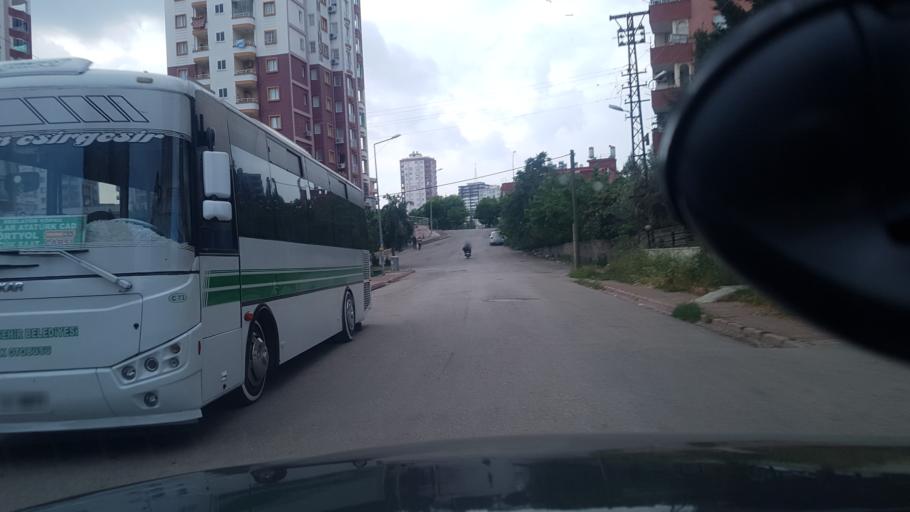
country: TR
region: Adana
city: Seyhan
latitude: 37.0278
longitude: 35.2881
